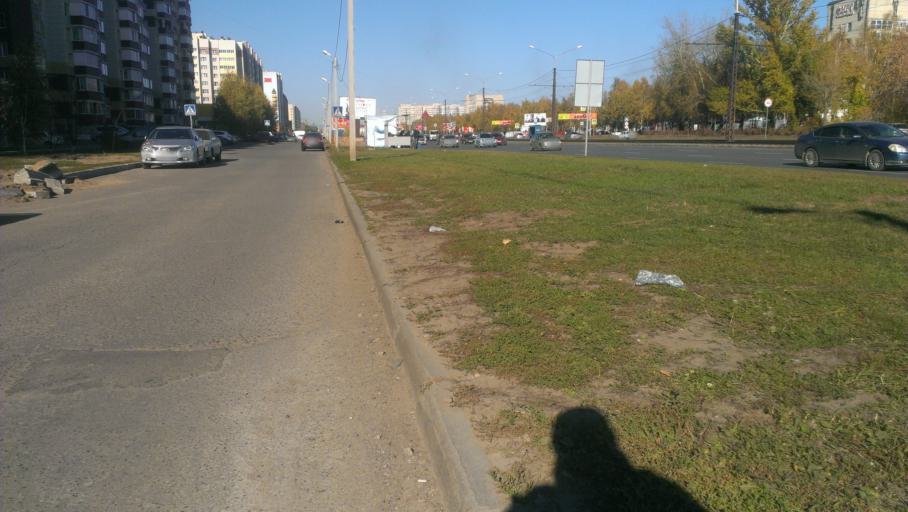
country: RU
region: Altai Krai
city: Novosilikatnyy
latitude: 53.3295
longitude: 83.6921
